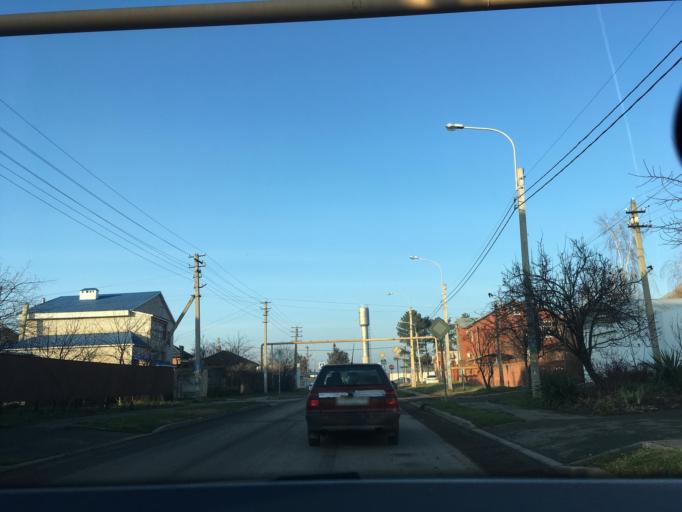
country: RU
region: Krasnodarskiy
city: Krasnodar
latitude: 45.1248
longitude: 39.0139
